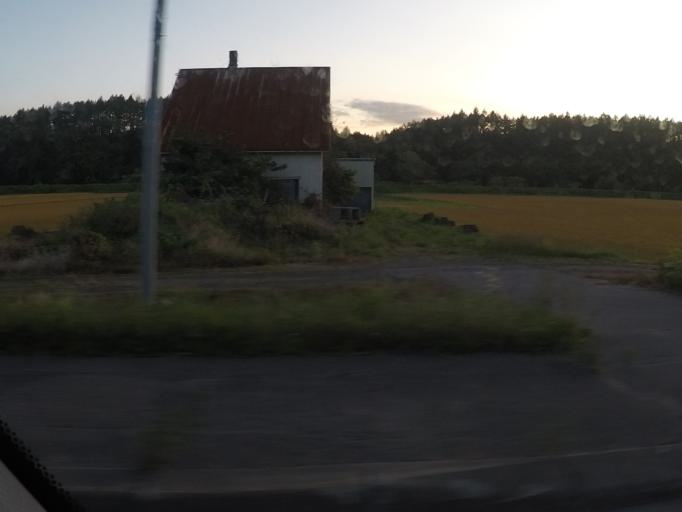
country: JP
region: Hokkaido
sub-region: Asahikawa-shi
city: Asahikawa
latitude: 43.6295
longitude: 142.4626
